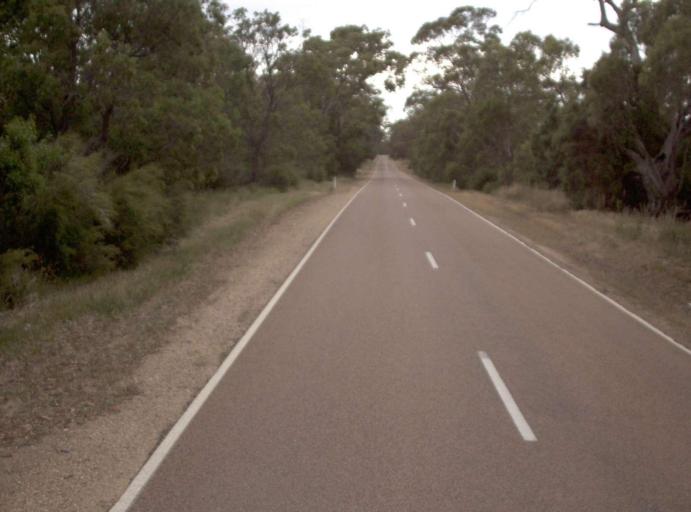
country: AU
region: Victoria
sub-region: Wellington
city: Sale
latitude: -38.0045
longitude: 147.2882
